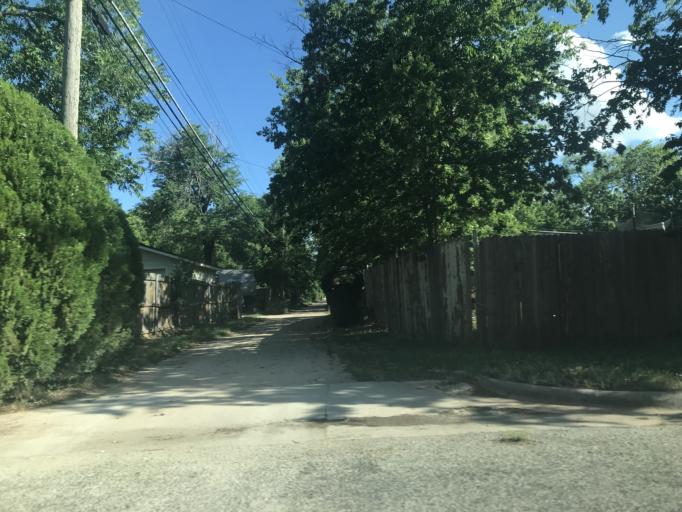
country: US
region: Texas
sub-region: Taylor County
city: Abilene
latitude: 32.4360
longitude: -99.7795
